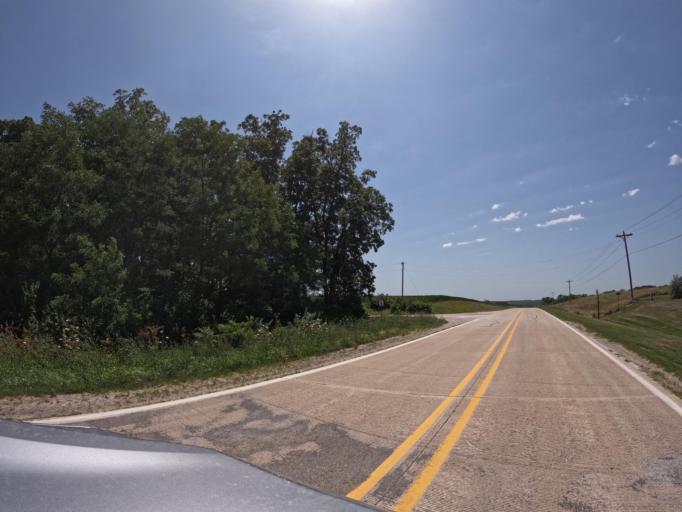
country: US
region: Iowa
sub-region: Henry County
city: Mount Pleasant
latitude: 40.9135
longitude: -91.5545
